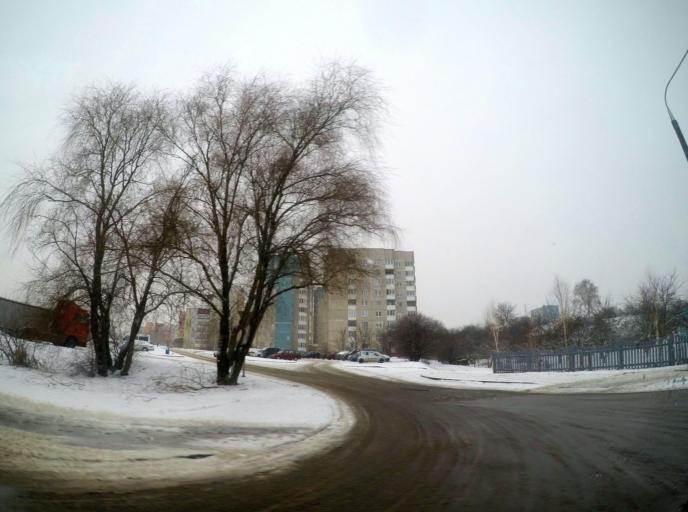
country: BY
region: Grodnenskaya
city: Hrodna
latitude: 53.7009
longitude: 23.8586
